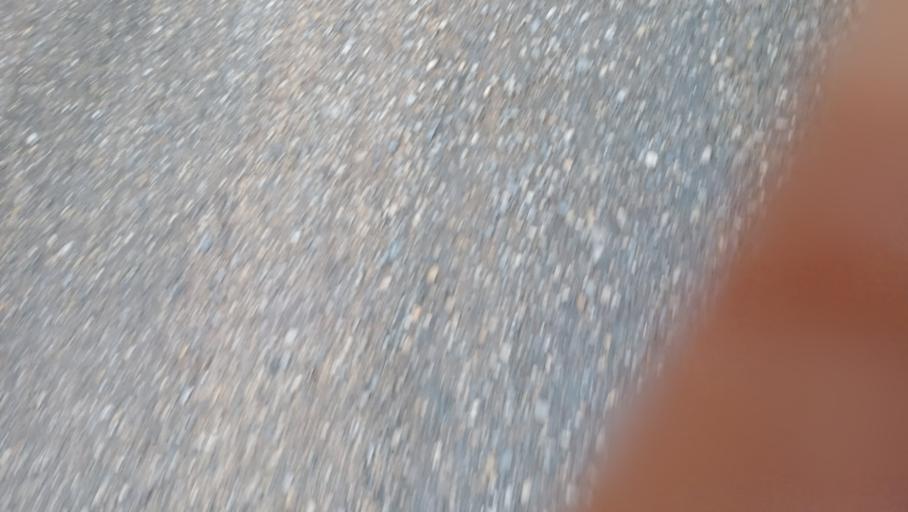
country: LA
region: Phongsali
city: Khoa
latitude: 21.0817
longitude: 102.5048
